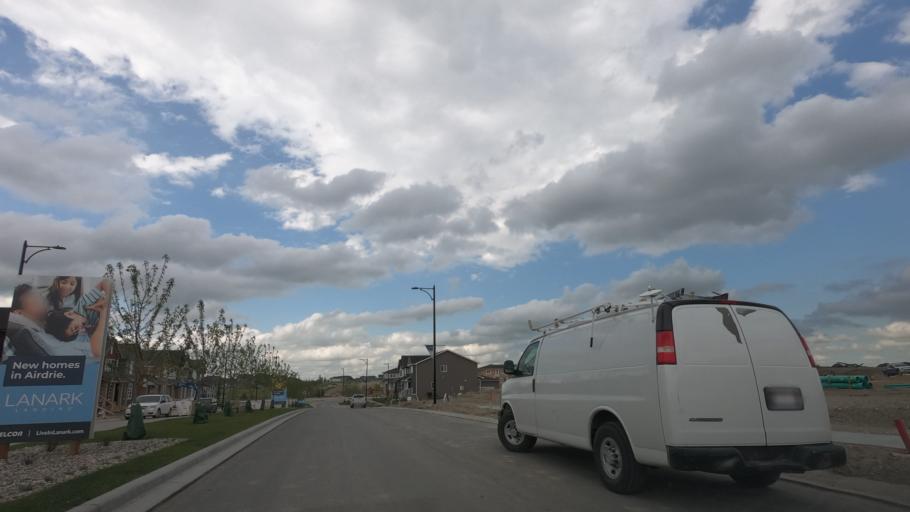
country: CA
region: Alberta
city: Airdrie
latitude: 51.2577
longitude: -113.9815
